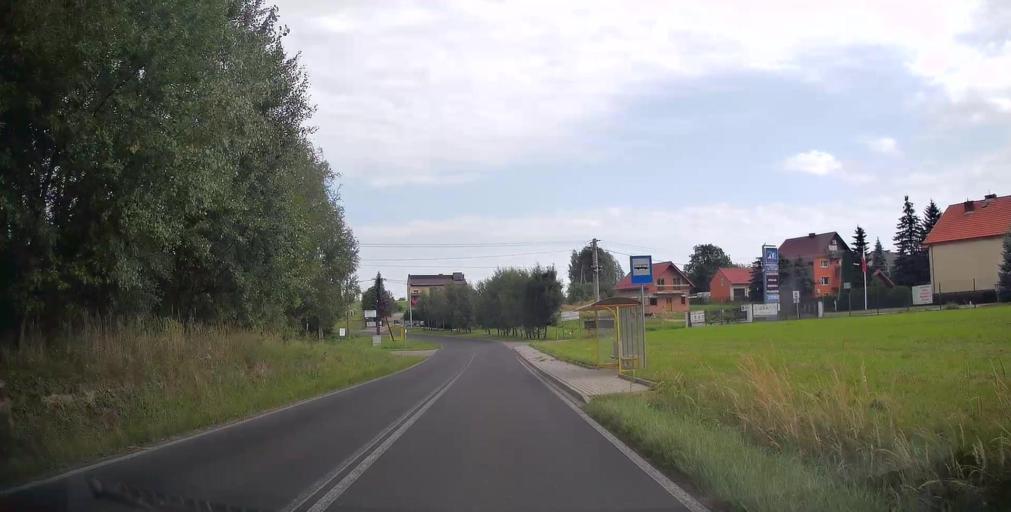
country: PL
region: Lesser Poland Voivodeship
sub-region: Powiat chrzanowski
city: Grojec
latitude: 50.0793
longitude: 19.5568
